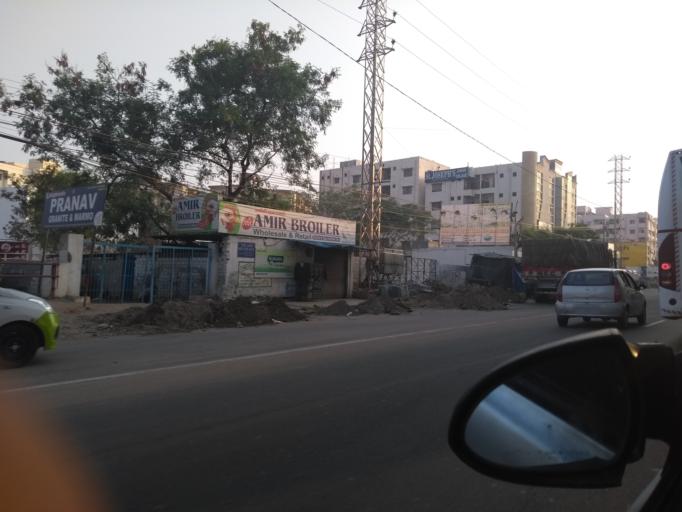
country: IN
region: Telangana
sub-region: Hyderabad
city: Hyderabad
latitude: 17.3530
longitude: 78.4188
